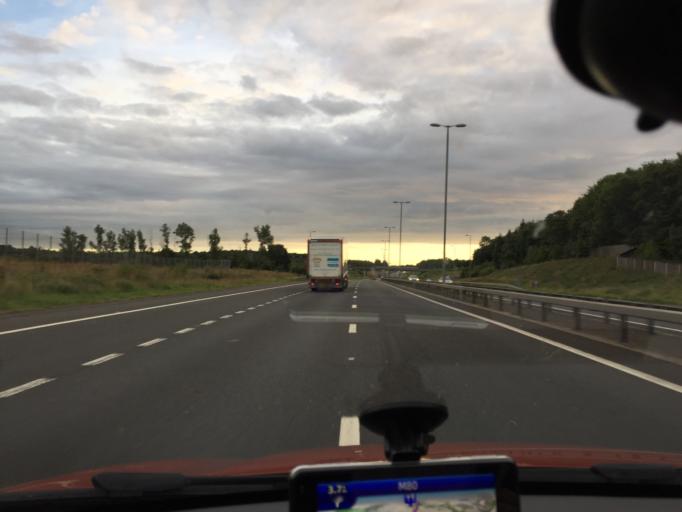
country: GB
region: Scotland
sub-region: North Lanarkshire
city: Cumbernauld
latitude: 55.9468
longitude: -4.0075
